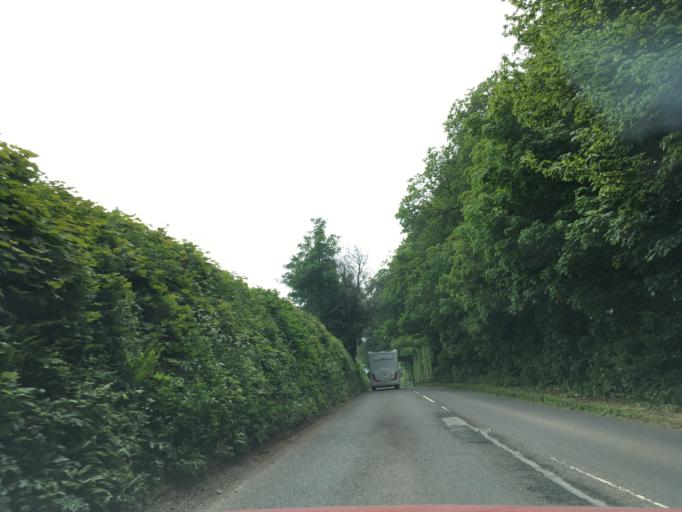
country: GB
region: England
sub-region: Devon
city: Totnes
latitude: 50.4115
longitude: -3.7076
